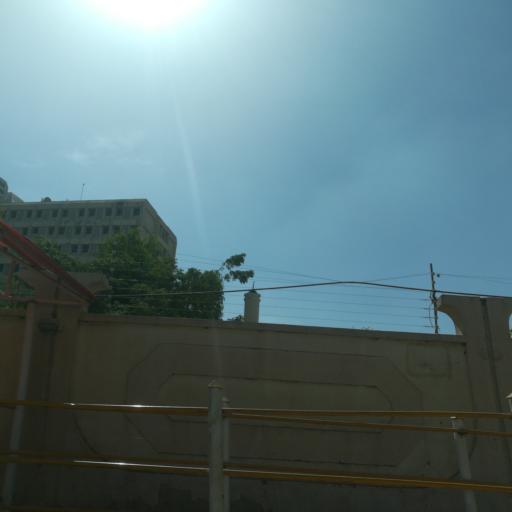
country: NG
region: Kano
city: Kano
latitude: 11.9926
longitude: 8.5319
